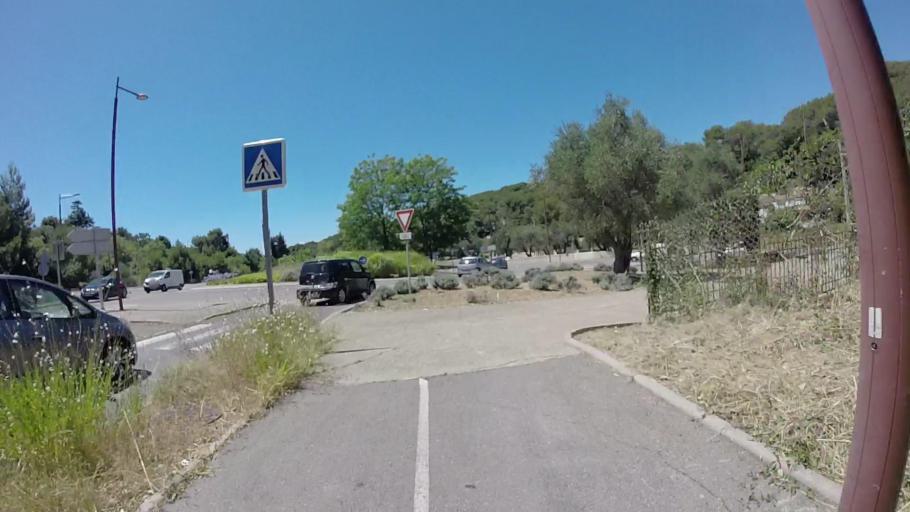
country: FR
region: Provence-Alpes-Cote d'Azur
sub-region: Departement des Alpes-Maritimes
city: Vallauris
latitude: 43.5863
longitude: 7.0911
